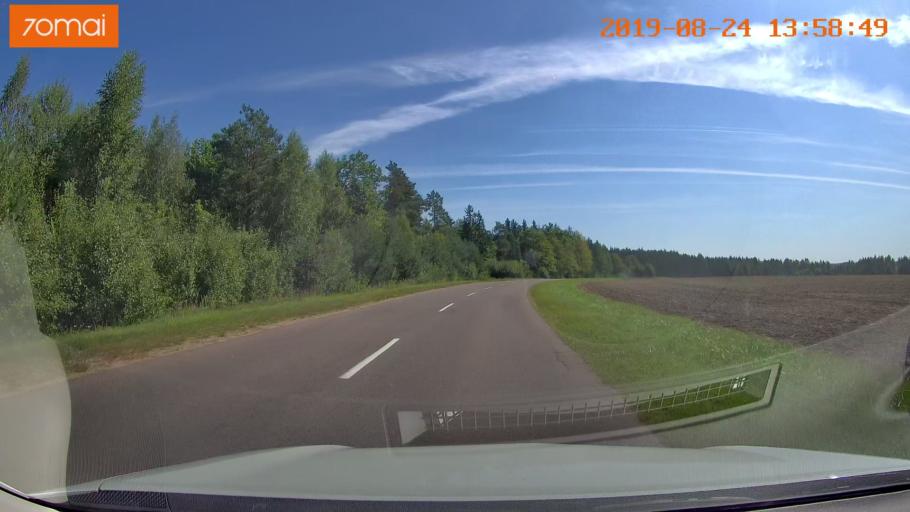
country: BY
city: Michanovichi
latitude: 53.6060
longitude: 27.6776
